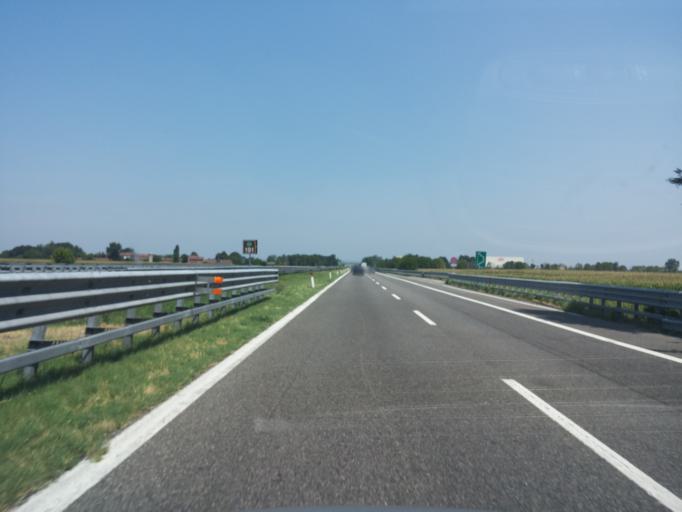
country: IT
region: Lombardy
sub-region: Provincia di Cremona
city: Persico Dosimo
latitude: 45.2000
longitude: 10.1010
